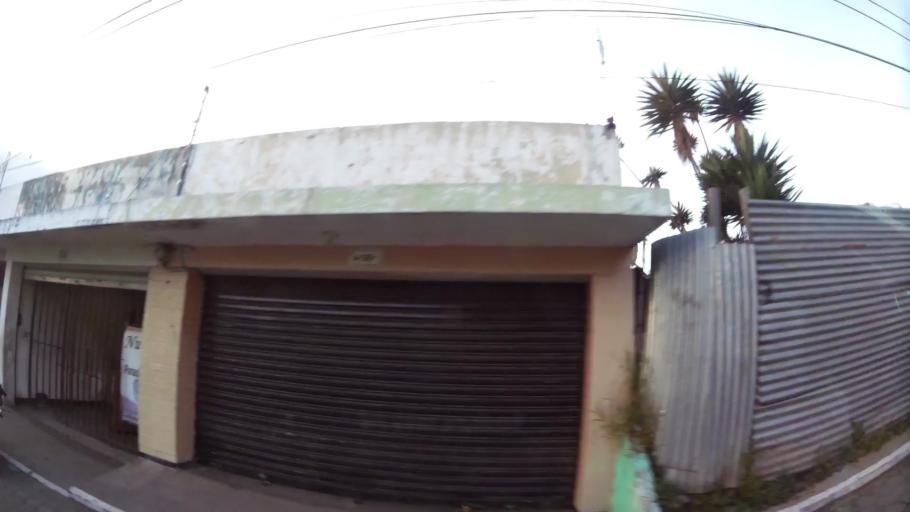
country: GT
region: Sacatepequez
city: San Lucas Sacatepequez
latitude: 14.6108
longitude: -90.6549
